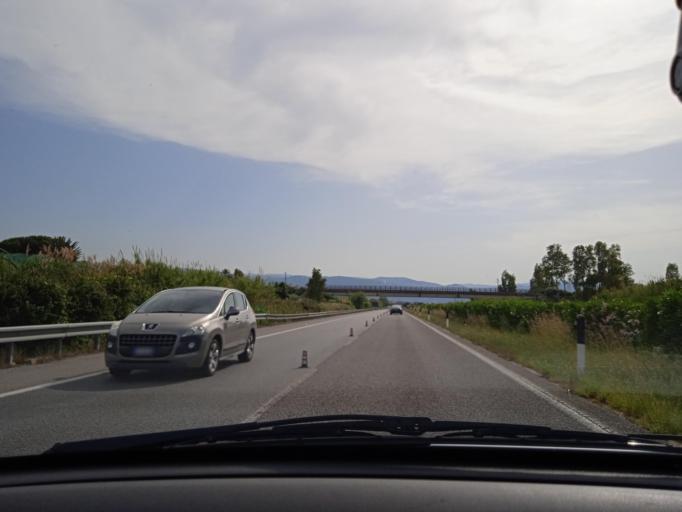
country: IT
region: Sicily
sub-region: Messina
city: Terme
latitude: 38.1408
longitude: 15.1587
